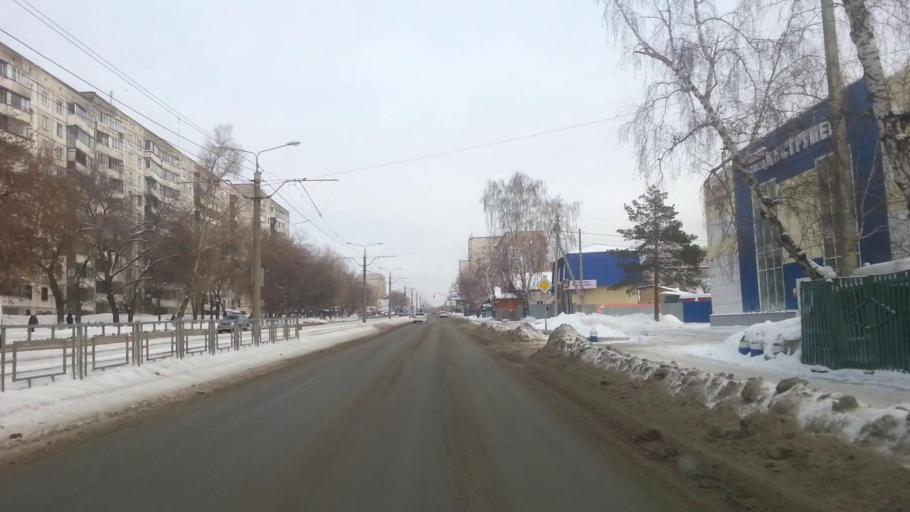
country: RU
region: Altai Krai
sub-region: Gorod Barnaulskiy
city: Barnaul
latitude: 53.3691
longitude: 83.7391
